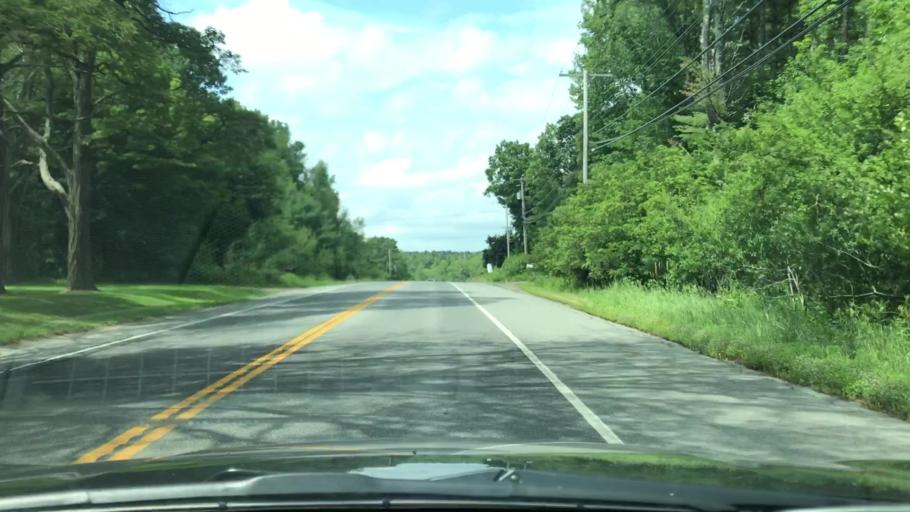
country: US
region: Maine
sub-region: Waldo County
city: Belfast
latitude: 44.3887
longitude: -68.9898
